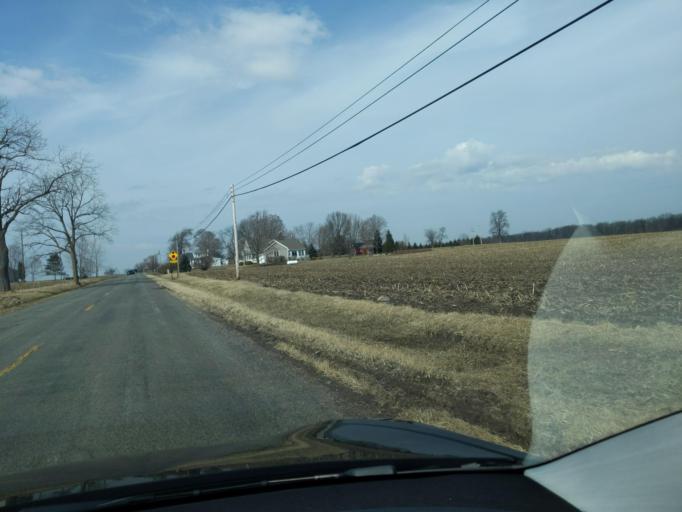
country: US
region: Michigan
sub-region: Ingham County
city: Williamston
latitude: 42.6588
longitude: -84.3085
